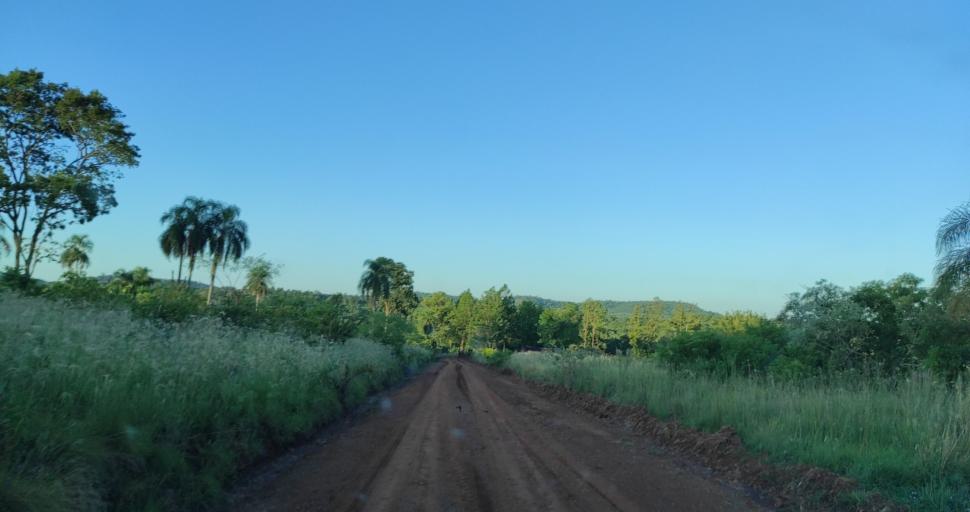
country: AR
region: Misiones
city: Gobernador Roca
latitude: -27.2172
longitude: -55.4141
